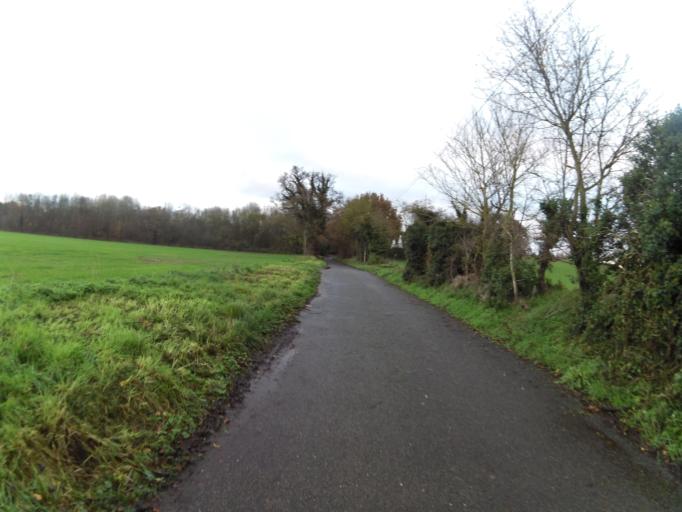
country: GB
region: England
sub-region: Suffolk
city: Bramford
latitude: 52.0583
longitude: 1.1023
